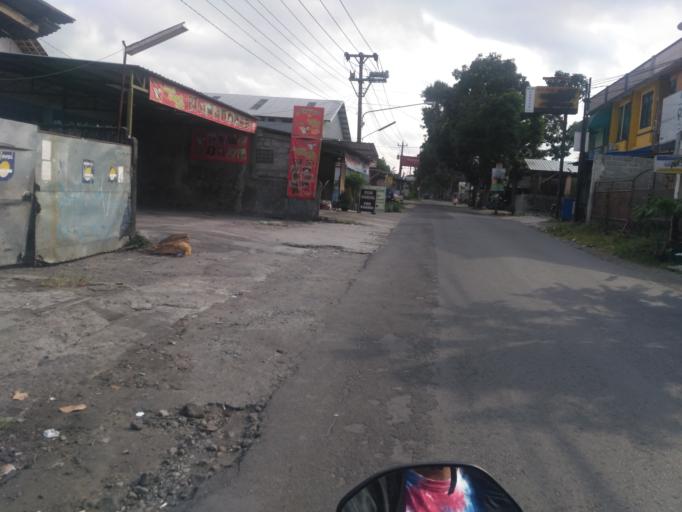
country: ID
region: Daerah Istimewa Yogyakarta
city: Yogyakarta
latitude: -7.7780
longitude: 110.3413
